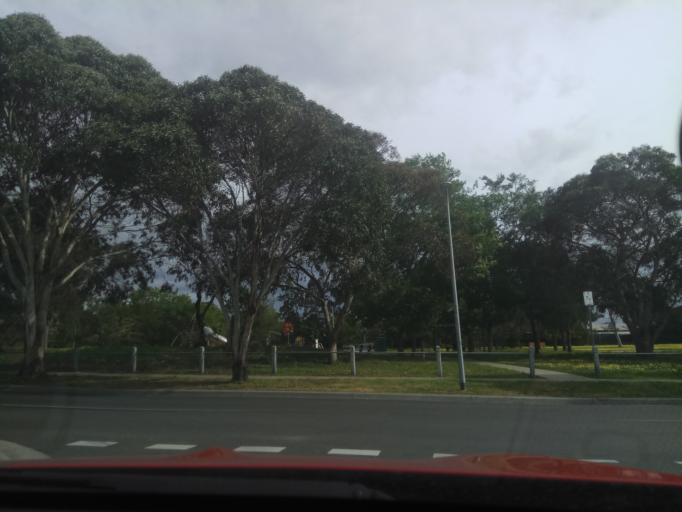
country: AU
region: Victoria
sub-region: Casey
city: Cranbourne North
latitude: -38.0701
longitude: 145.2734
